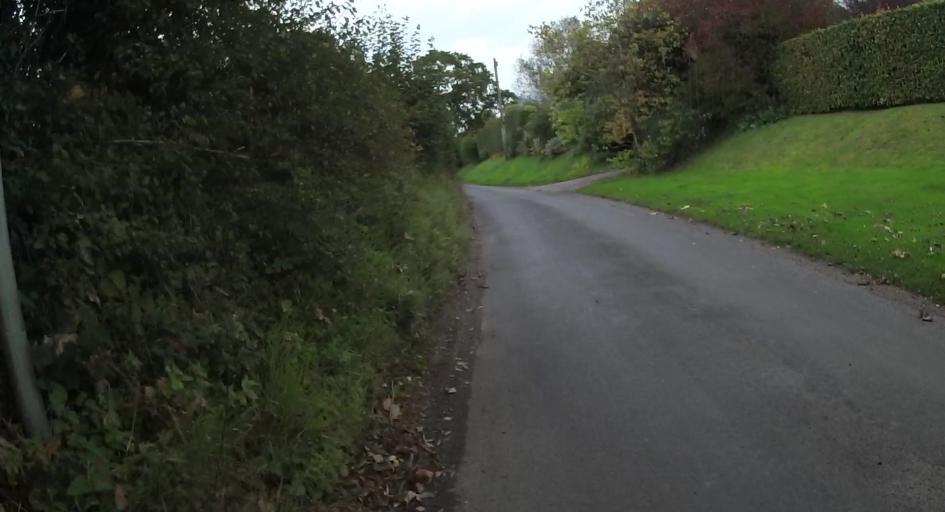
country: GB
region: England
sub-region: Hampshire
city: Alton
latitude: 51.1380
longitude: -0.9304
